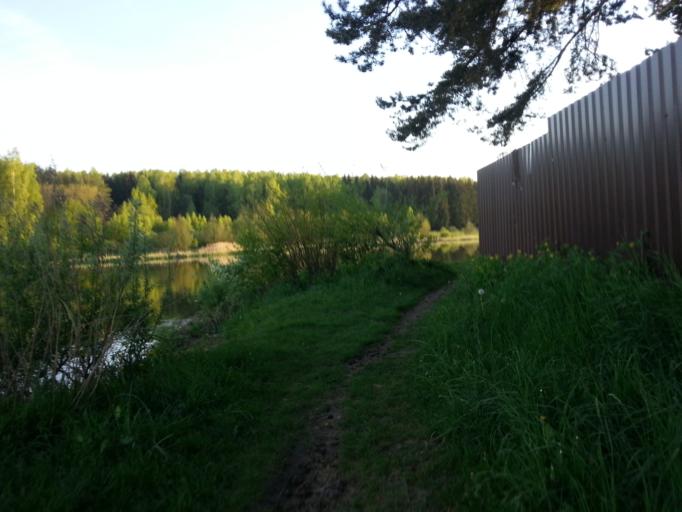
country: BY
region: Minsk
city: Slabada
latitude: 54.0494
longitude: 27.8718
